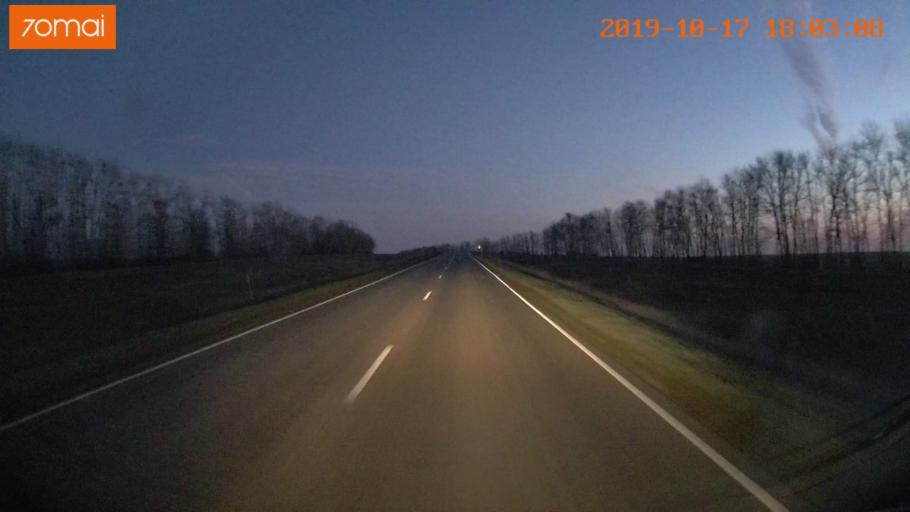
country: RU
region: Tula
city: Kurkino
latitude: 53.4983
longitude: 38.6210
